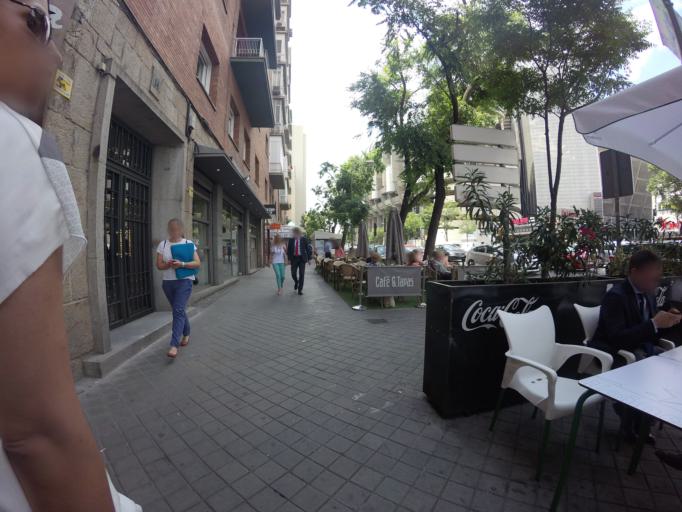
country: ES
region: Madrid
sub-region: Provincia de Madrid
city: Chamartin
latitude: 40.4516
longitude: -3.6866
